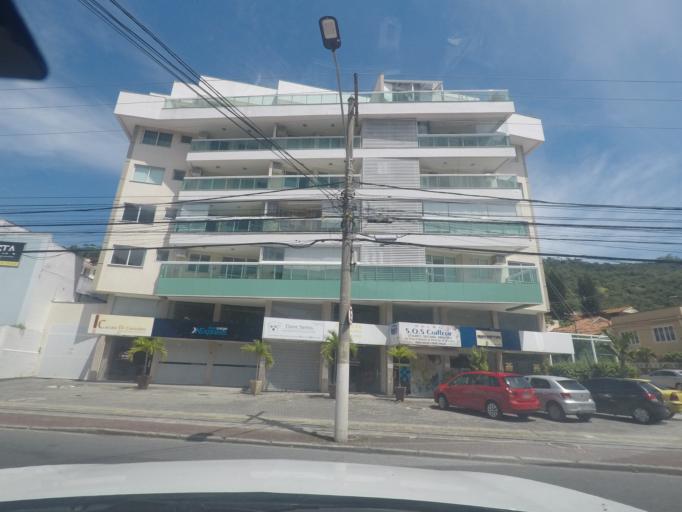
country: BR
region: Rio de Janeiro
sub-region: Niteroi
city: Niteroi
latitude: -22.9150
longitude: -43.0831
